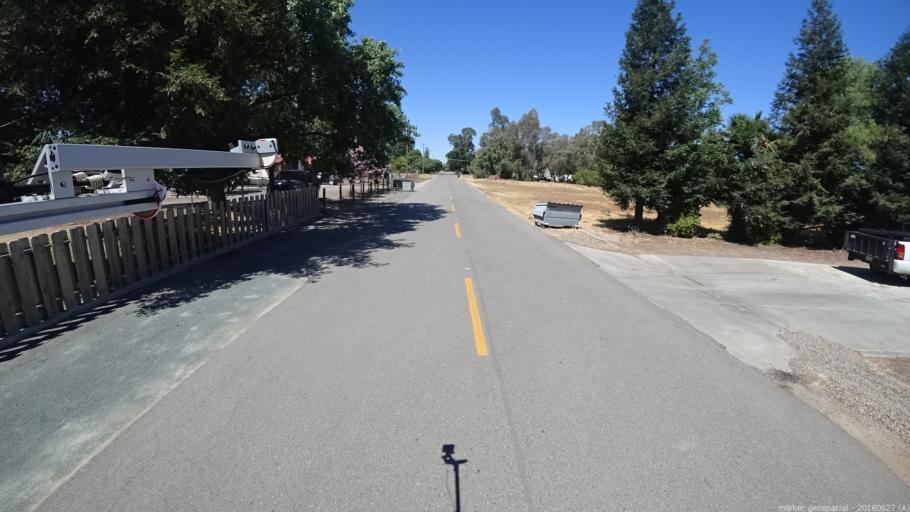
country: US
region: California
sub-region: Madera County
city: Bonadelle Ranchos-Madera Ranchos
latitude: 36.9213
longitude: -119.8805
